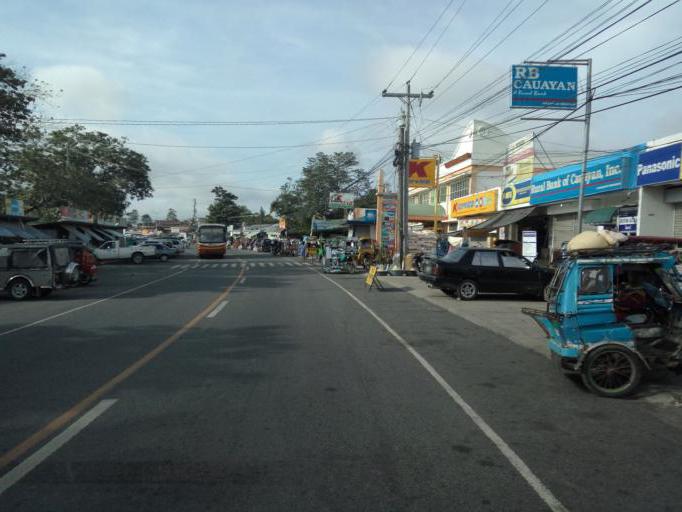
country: PH
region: Cagayan Valley
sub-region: Province of Isabela
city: Cabagan
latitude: 17.4282
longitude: 121.7728
